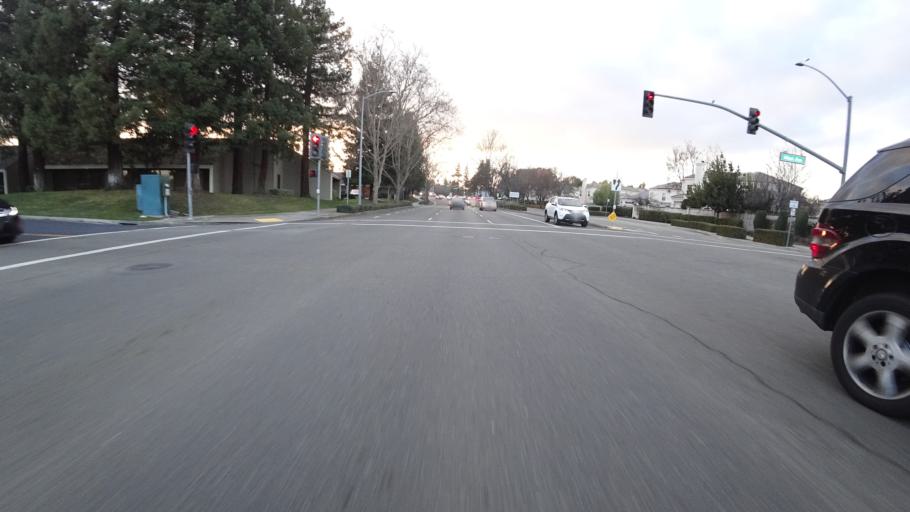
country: US
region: California
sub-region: Alameda County
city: Pleasanton
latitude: 37.6880
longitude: -121.8758
